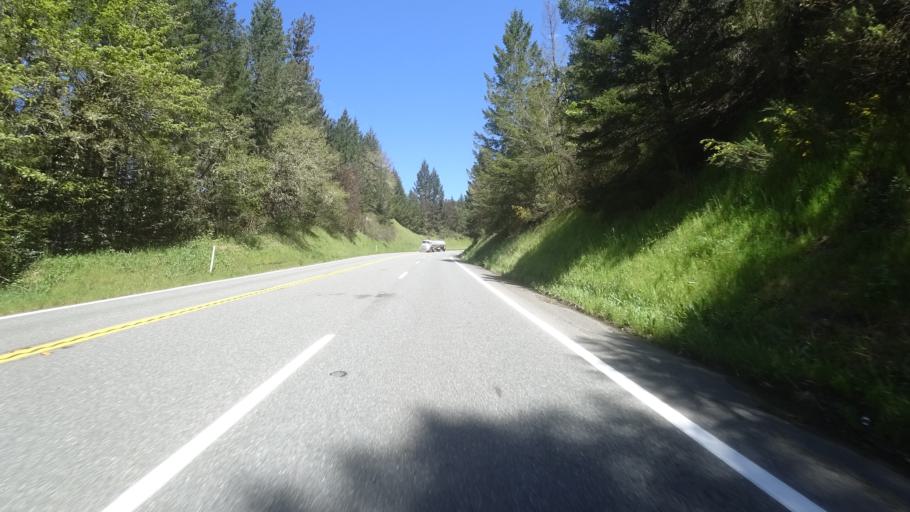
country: US
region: California
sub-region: Humboldt County
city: Blue Lake
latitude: 40.9116
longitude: -123.8092
